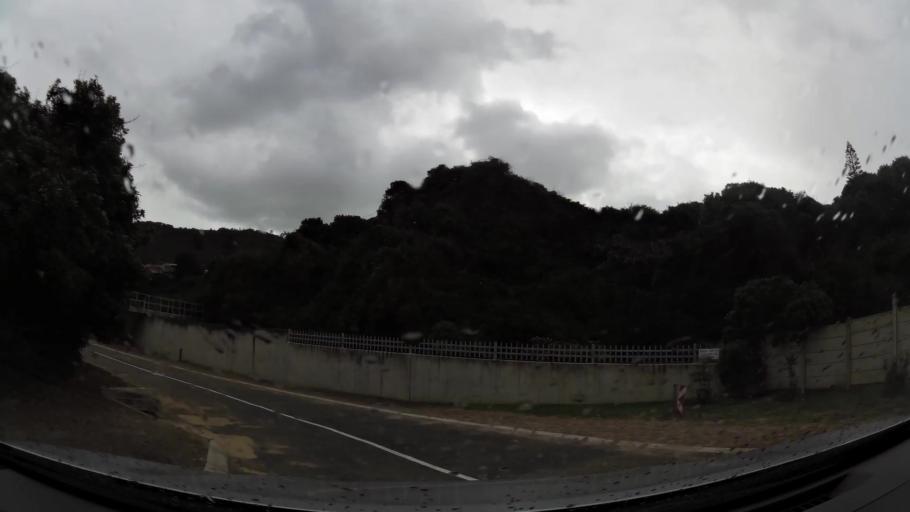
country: ZA
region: Western Cape
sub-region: Eden District Municipality
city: George
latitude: -34.0491
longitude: 22.3108
